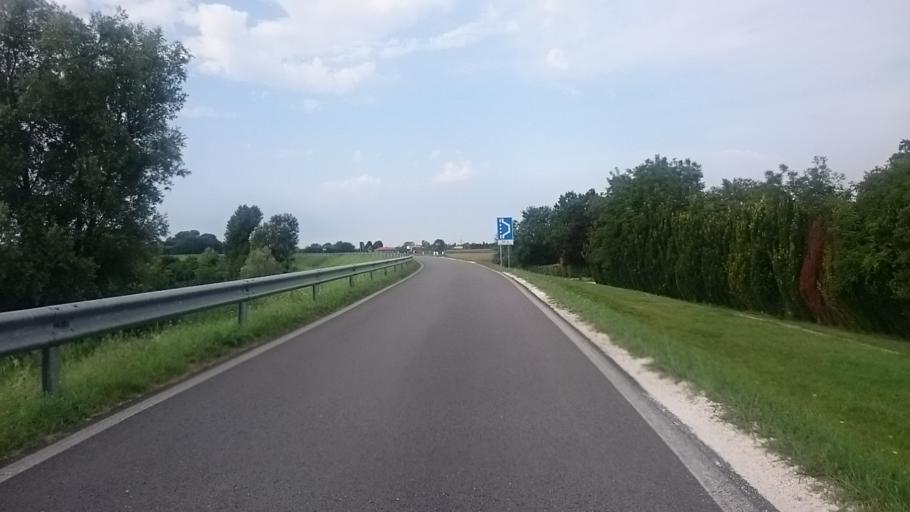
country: IT
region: Veneto
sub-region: Provincia di Padova
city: Polverara
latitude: 45.3168
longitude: 11.9354
